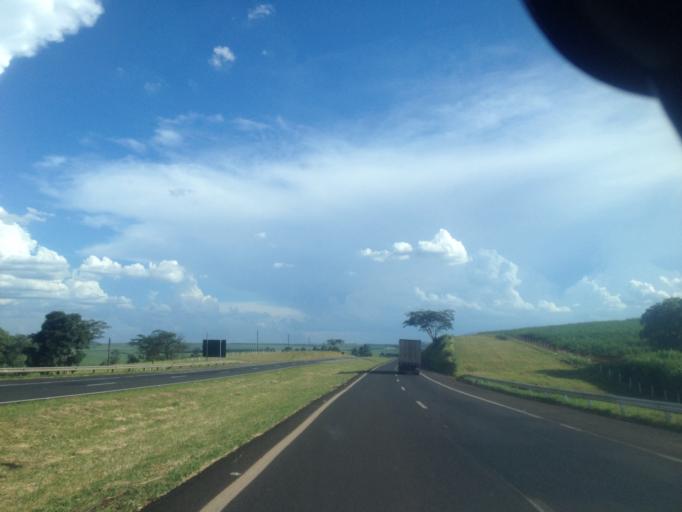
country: BR
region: Sao Paulo
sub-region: Sao Simao
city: Sao Simao
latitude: -21.4733
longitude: -47.6403
